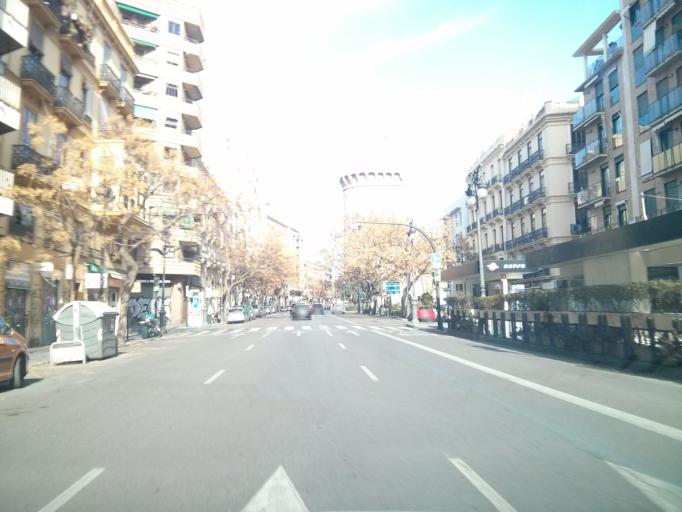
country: ES
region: Valencia
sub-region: Provincia de Valencia
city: Valencia
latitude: 39.4741
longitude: -0.3838
